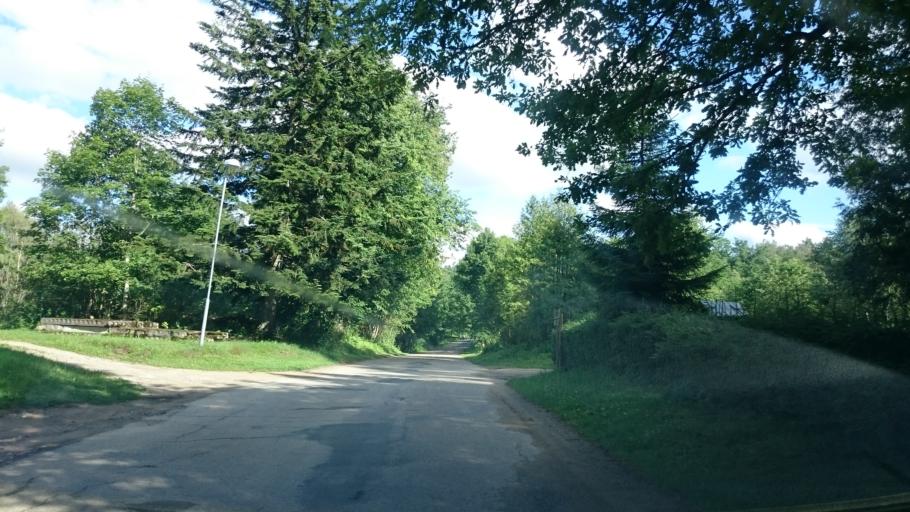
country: LV
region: Aizpute
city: Aizpute
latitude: 56.7165
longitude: 21.5967
